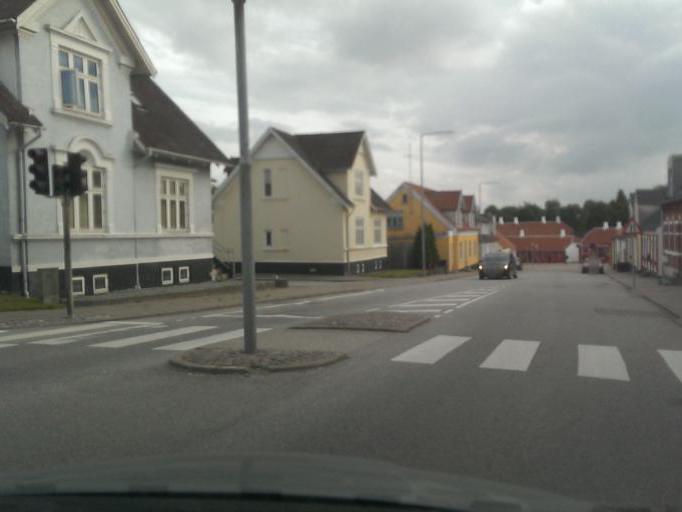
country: DK
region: North Denmark
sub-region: Hjorring Kommune
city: Hjorring
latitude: 57.4652
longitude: 9.9836
